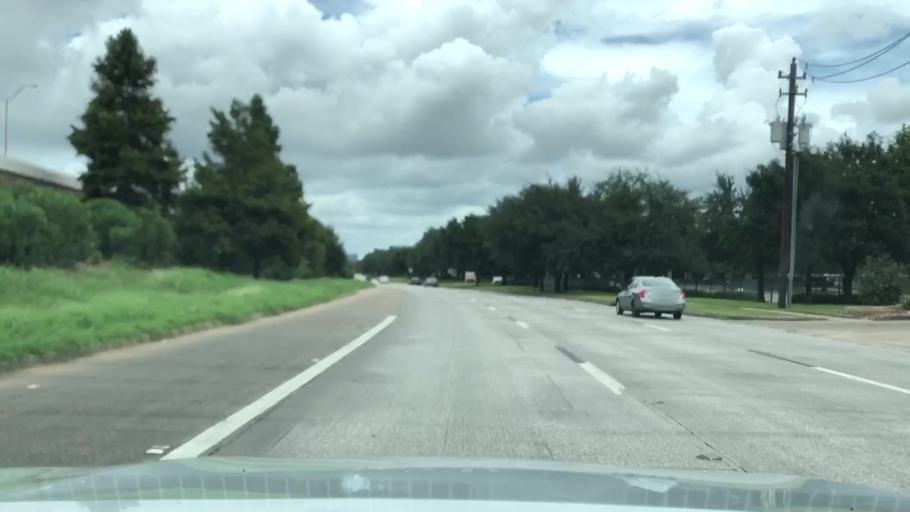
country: US
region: Texas
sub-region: Fort Bend County
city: Meadows Place
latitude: 29.6898
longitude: -95.5569
